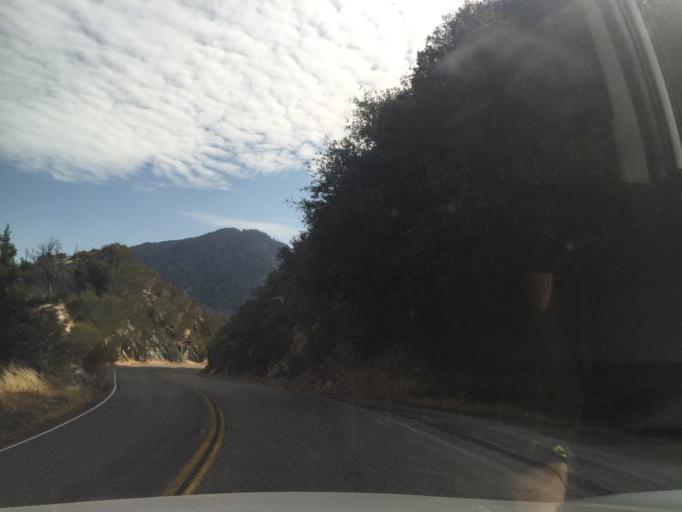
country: US
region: California
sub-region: Los Angeles County
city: Altadena
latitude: 34.2635
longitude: -118.0999
